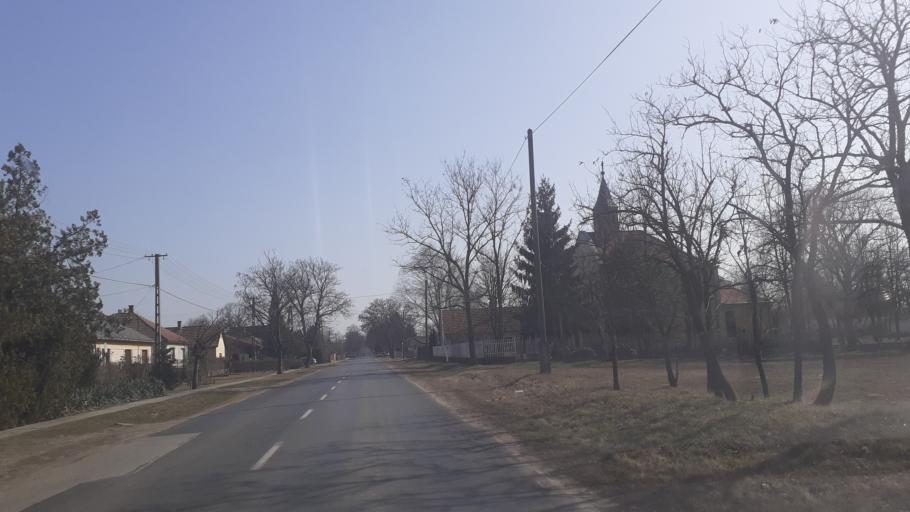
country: HU
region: Bacs-Kiskun
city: Lajosmizse
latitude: 46.9771
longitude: 19.5752
